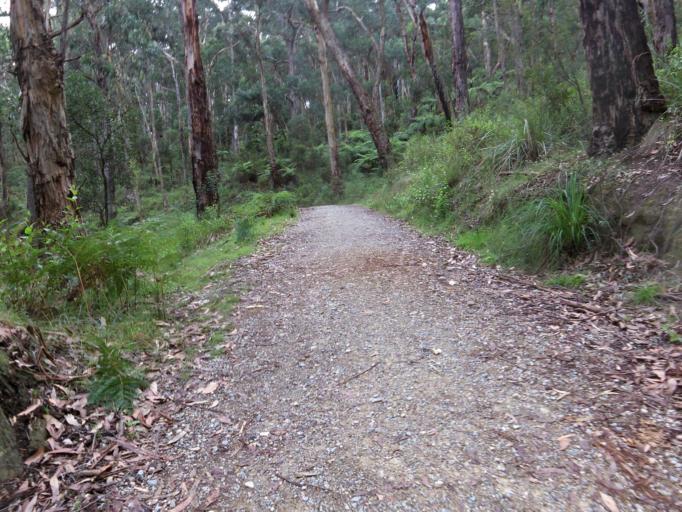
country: AU
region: Victoria
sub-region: Knox
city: The Basin
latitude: -37.8412
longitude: 145.3398
